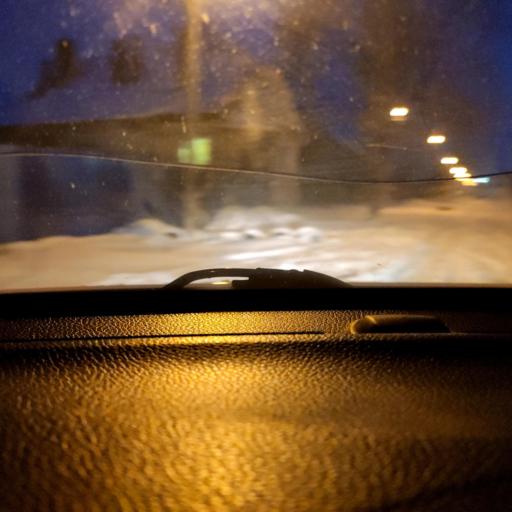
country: RU
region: Voronezj
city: Voronezh
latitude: 51.7361
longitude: 39.2619
